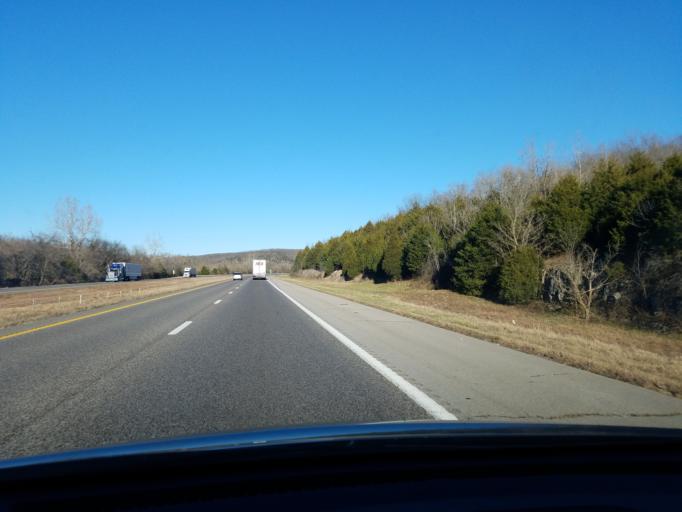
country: US
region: Missouri
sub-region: Pulaski County
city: Saint Robert
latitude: 37.8567
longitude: -92.0732
